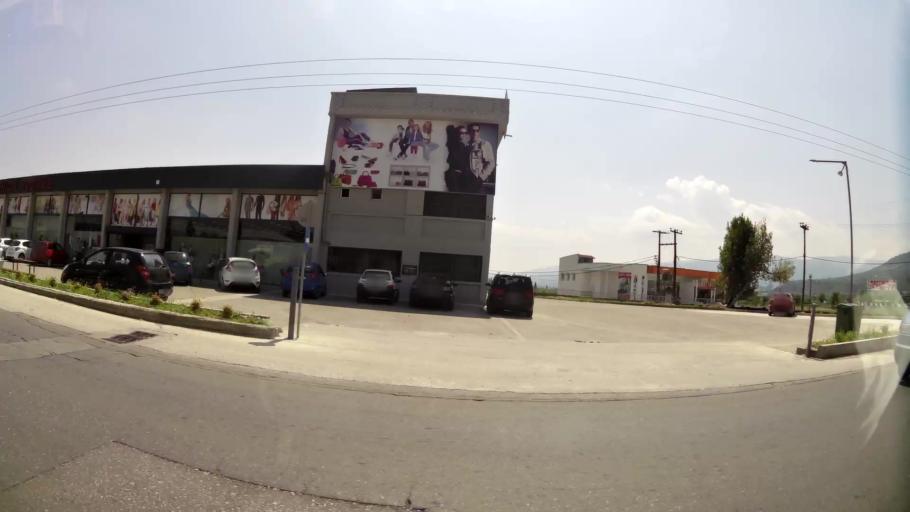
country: GR
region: Central Macedonia
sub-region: Nomos Imathias
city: Veroia
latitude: 40.5238
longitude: 22.2147
